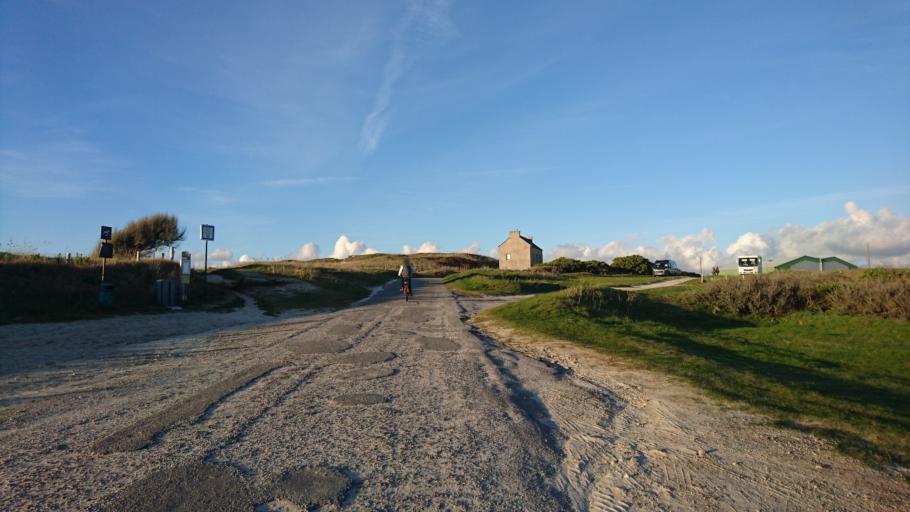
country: FR
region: Brittany
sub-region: Departement du Finistere
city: Lampaul-Plouarzel
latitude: 48.4471
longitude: -4.7773
